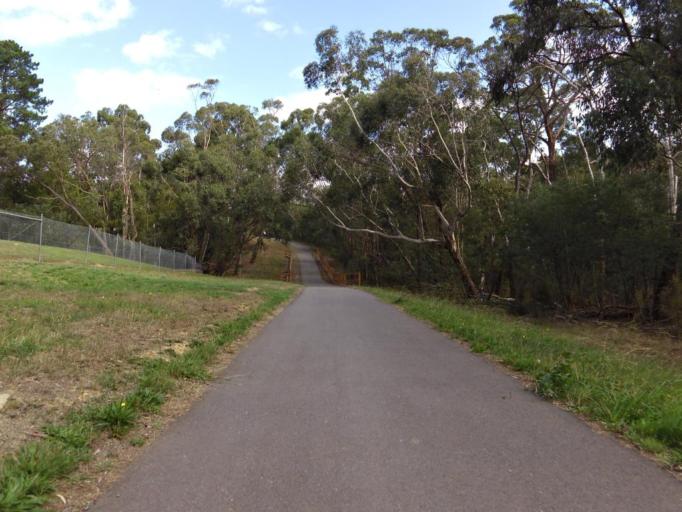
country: AU
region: Victoria
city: Mitcham
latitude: -37.7984
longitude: 145.2037
